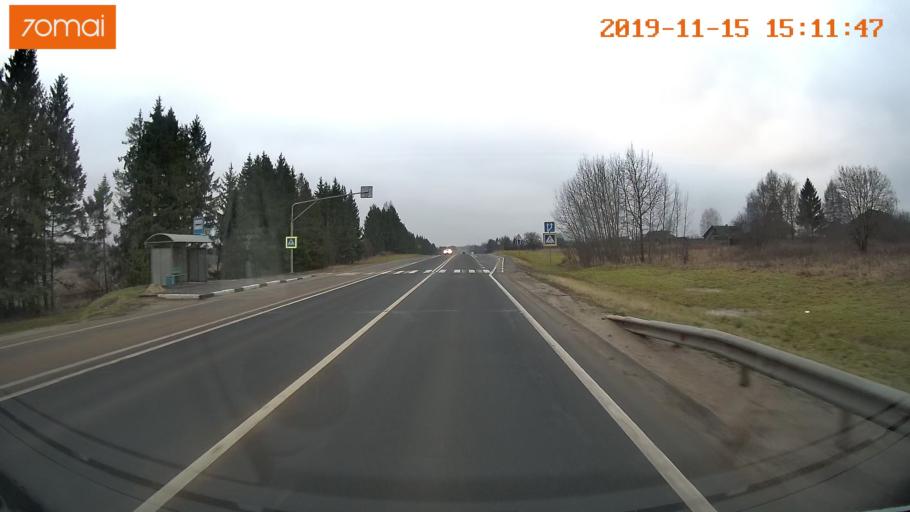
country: RU
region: Jaroslavl
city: Prechistoye
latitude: 58.3322
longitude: 40.2361
